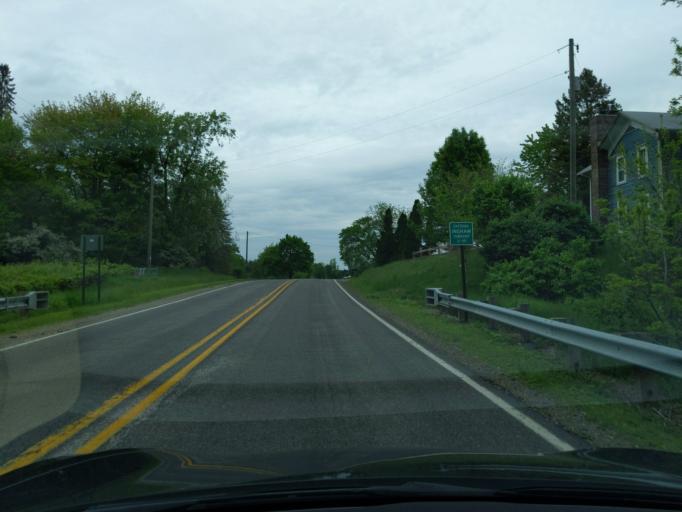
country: US
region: Michigan
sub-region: Ingham County
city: Leslie
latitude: 42.5122
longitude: -84.3562
